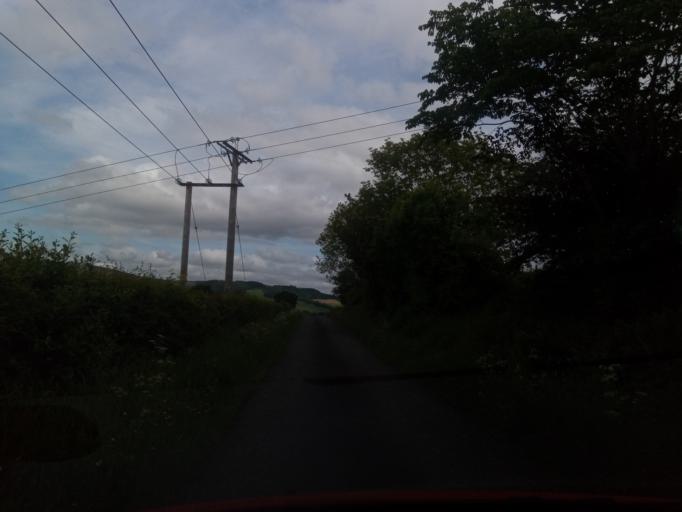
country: GB
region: Scotland
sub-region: The Scottish Borders
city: Selkirk
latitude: 55.5309
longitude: -2.8739
